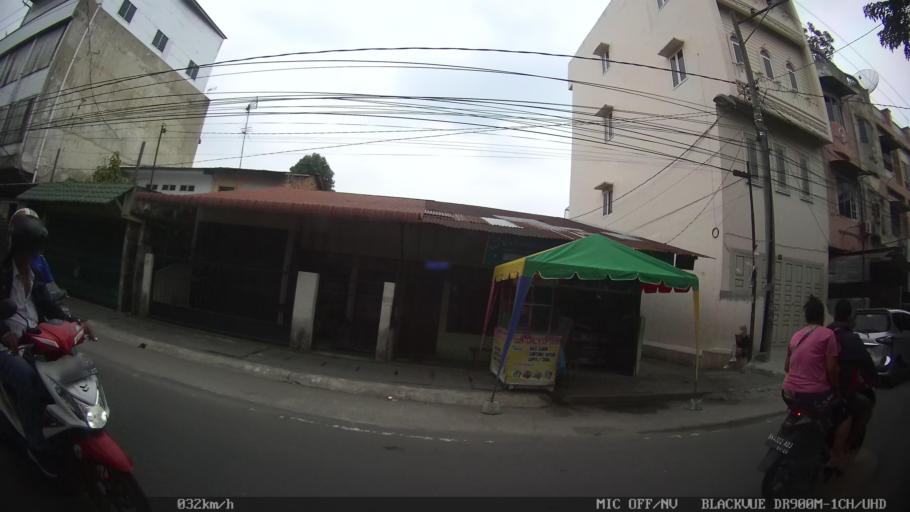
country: ID
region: North Sumatra
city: Medan
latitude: 3.5630
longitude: 98.6900
